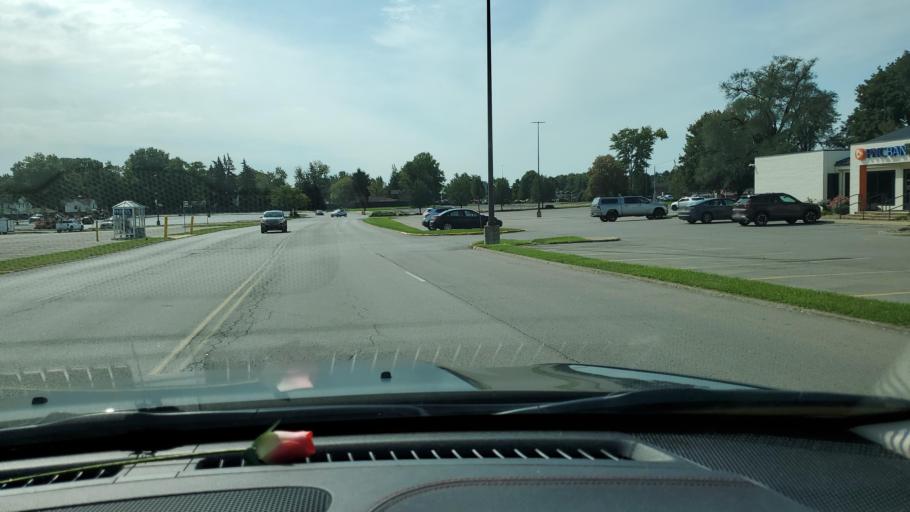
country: US
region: Ohio
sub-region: Mahoning County
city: Boardman
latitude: 41.0203
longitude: -80.6616
